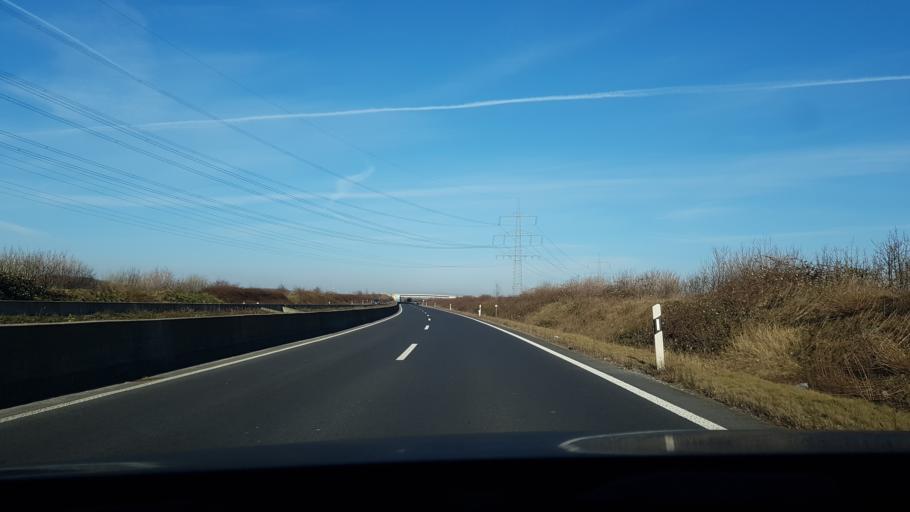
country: DE
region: North Rhine-Westphalia
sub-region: Regierungsbezirk Dusseldorf
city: Ratingen
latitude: 51.3223
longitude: 6.7601
